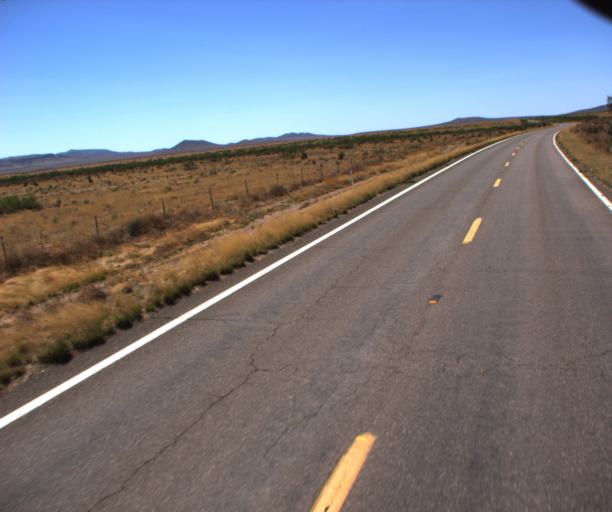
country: US
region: Arizona
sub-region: Cochise County
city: Douglas
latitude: 31.6869
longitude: -109.1350
